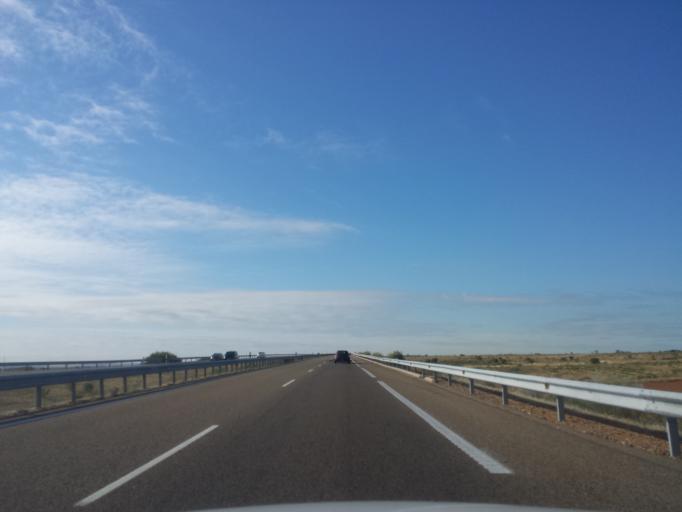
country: ES
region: Castille and Leon
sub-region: Provincia de Leon
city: Valdevimbre
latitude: 42.3810
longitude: -5.5952
